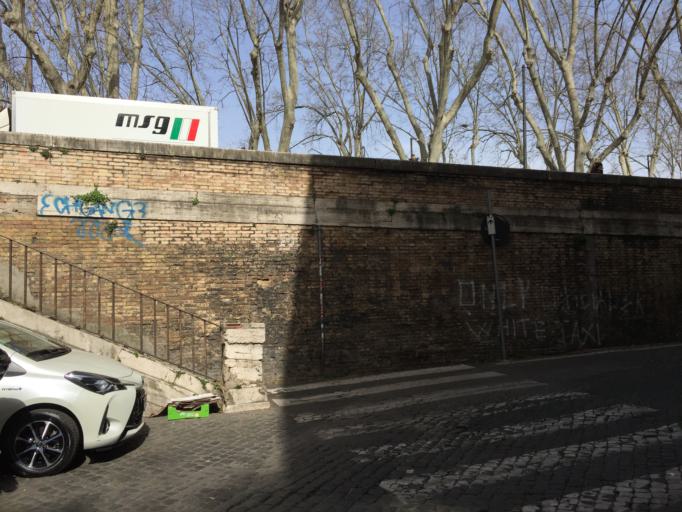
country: VA
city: Vatican City
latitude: 41.9018
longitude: 12.4722
